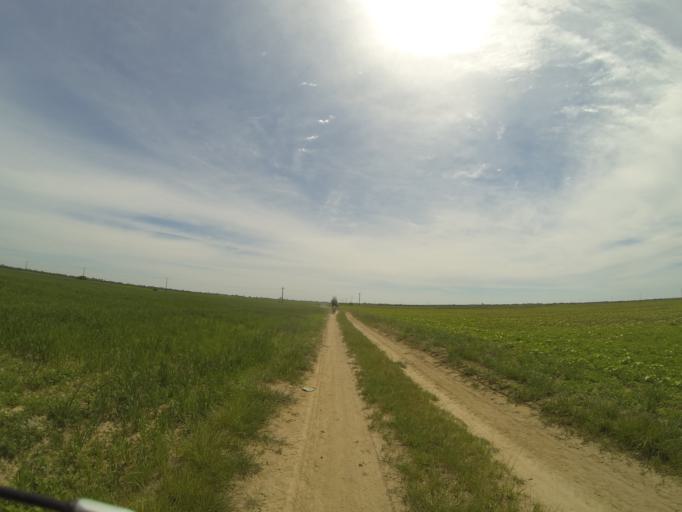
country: RO
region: Dolj
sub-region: Comuna Ghindeni
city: Ghindeni
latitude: 44.2064
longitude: 23.9559
